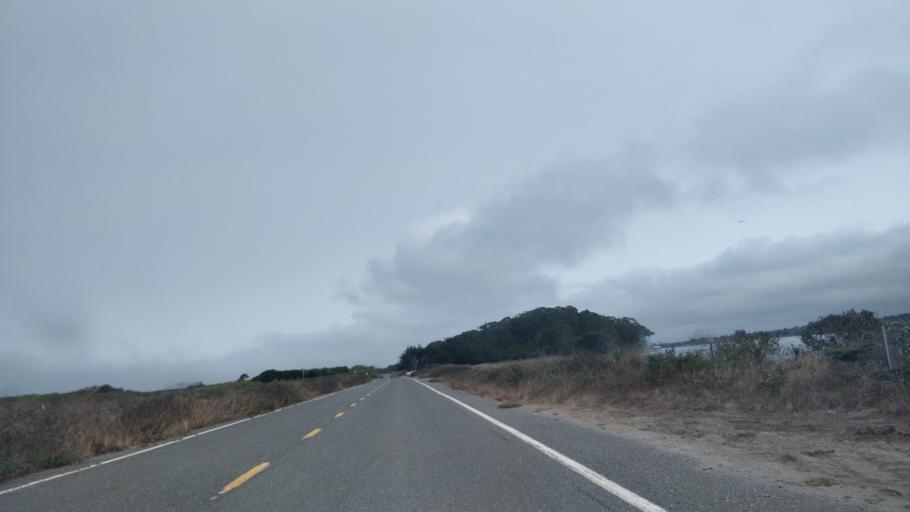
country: US
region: California
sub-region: Humboldt County
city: Bayview
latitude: 40.7733
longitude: -124.2131
